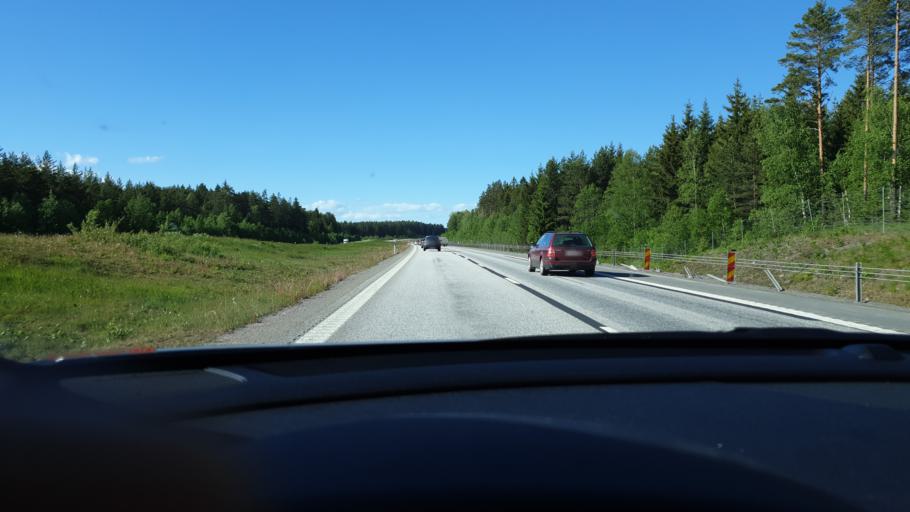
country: SE
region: Uppsala
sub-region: Tierps Kommun
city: Tierp
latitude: 60.2703
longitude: 17.5016
